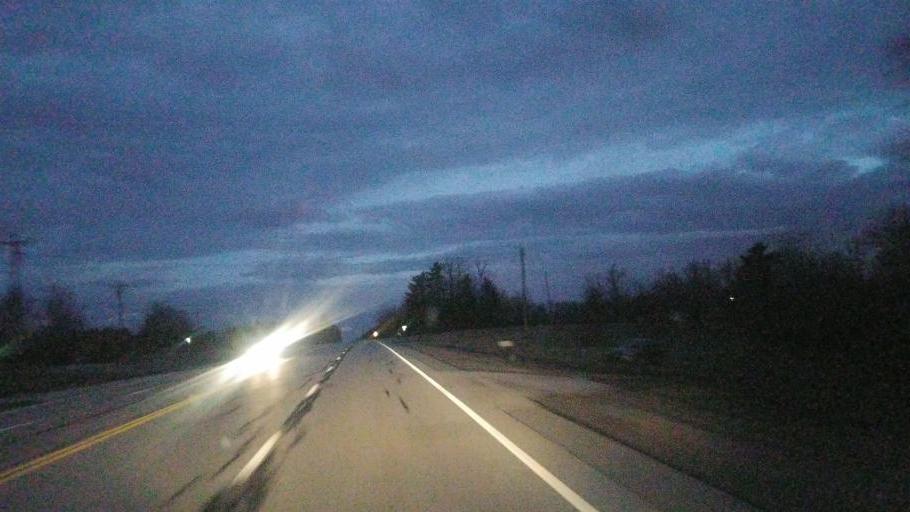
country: US
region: Tennessee
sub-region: Sequatchie County
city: Dunlap
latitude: 35.4795
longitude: -85.4635
